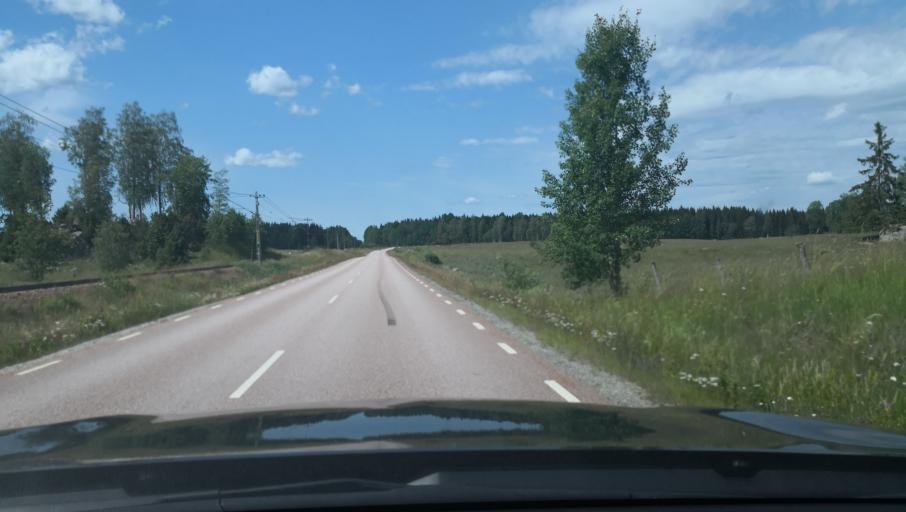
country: SE
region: Vaestmanland
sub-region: Surahammars Kommun
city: Ramnas
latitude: 59.8386
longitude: 16.1246
